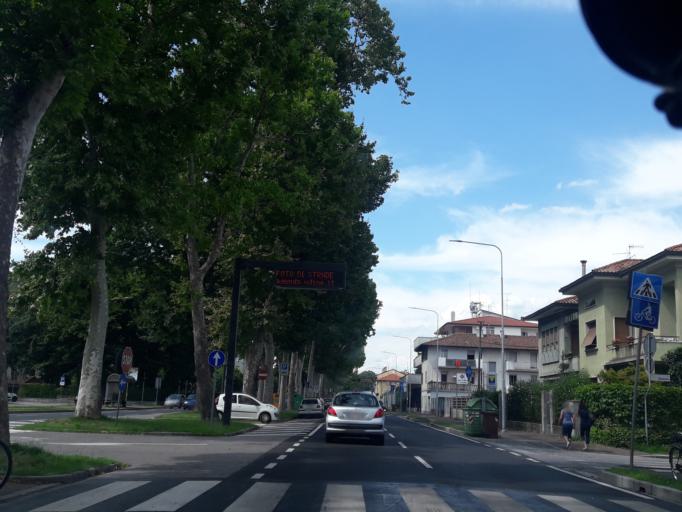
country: IT
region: Friuli Venezia Giulia
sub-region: Provincia di Udine
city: Udine
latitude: 46.0656
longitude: 13.2460
